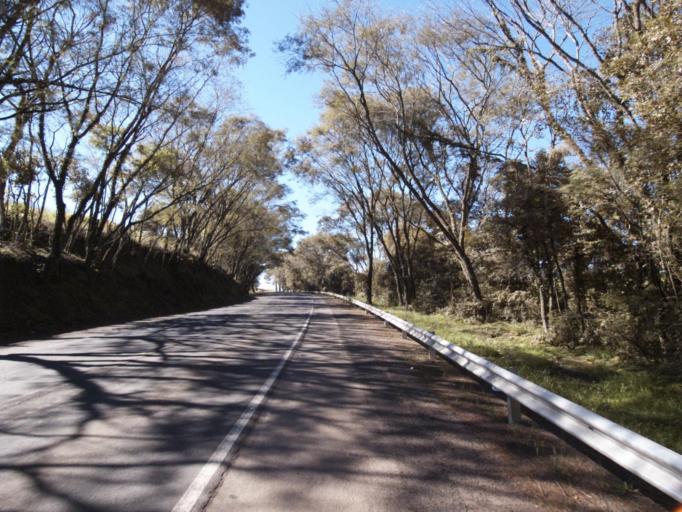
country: BR
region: Santa Catarina
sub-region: Sao Lourenco Do Oeste
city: Sao Lourenco dOeste
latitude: -26.8278
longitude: -53.0789
